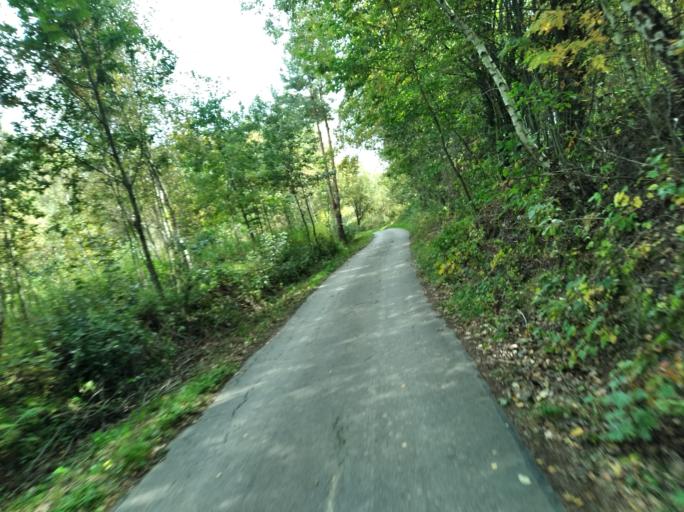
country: PL
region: Subcarpathian Voivodeship
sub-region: Powiat strzyzowski
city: Jawornik
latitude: 49.8384
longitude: 21.8820
